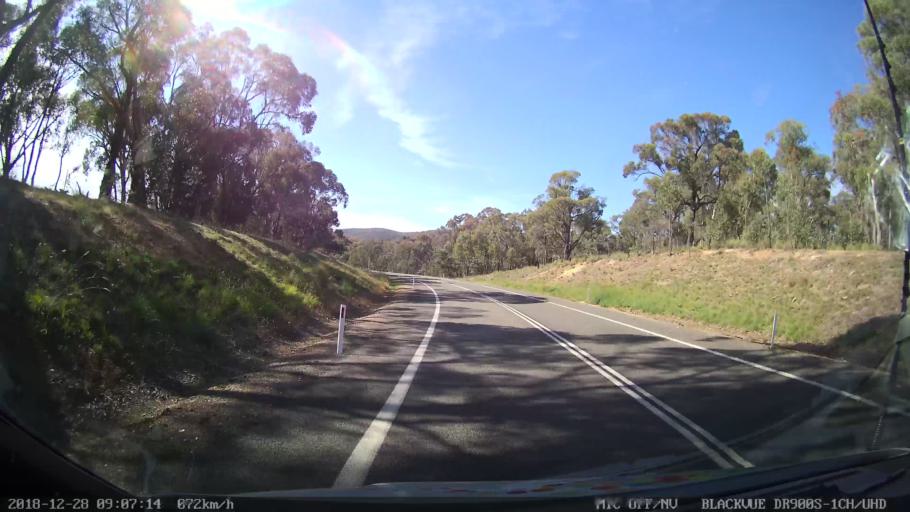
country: AU
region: New South Wales
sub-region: Upper Lachlan Shire
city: Crookwell
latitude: -34.2045
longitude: 149.3444
